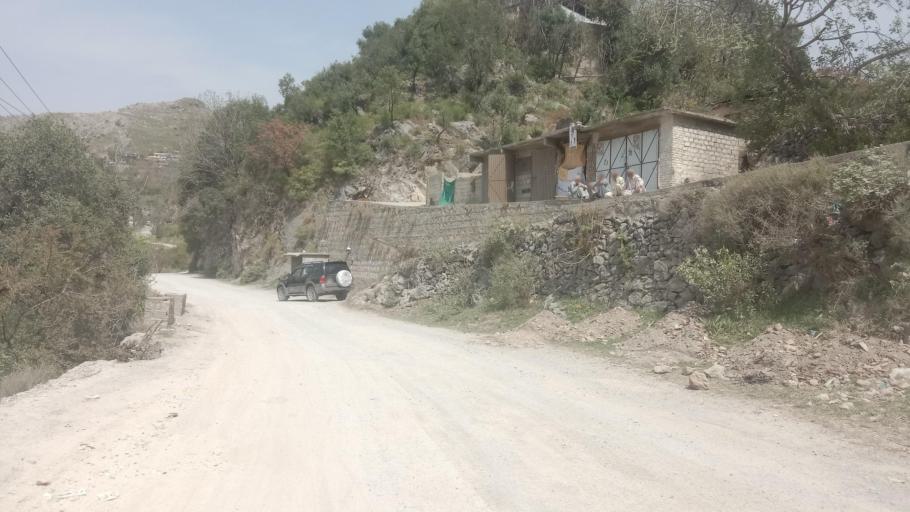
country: PK
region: Khyber Pakhtunkhwa
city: Abbottabad
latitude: 34.1632
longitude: 73.2822
